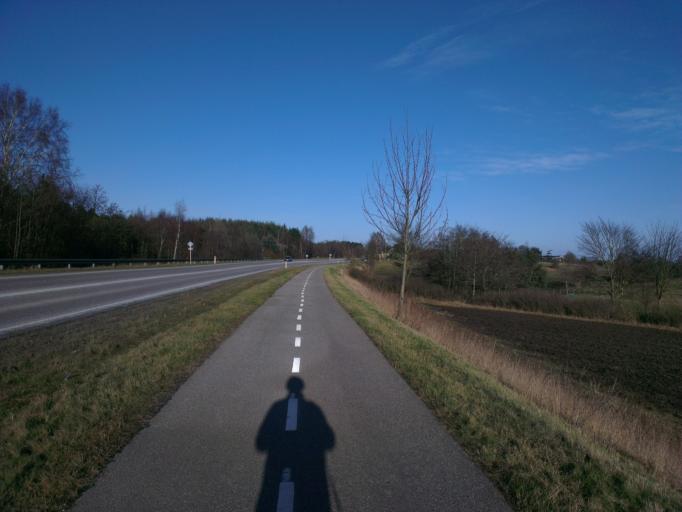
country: DK
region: Capital Region
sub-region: Frederikssund Kommune
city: Jaegerspris
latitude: 55.8153
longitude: 11.9969
